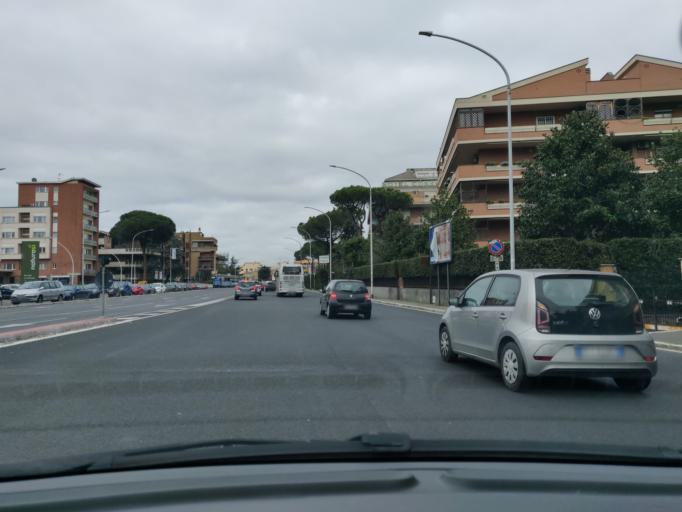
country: VA
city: Vatican City
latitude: 41.8910
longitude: 12.4131
